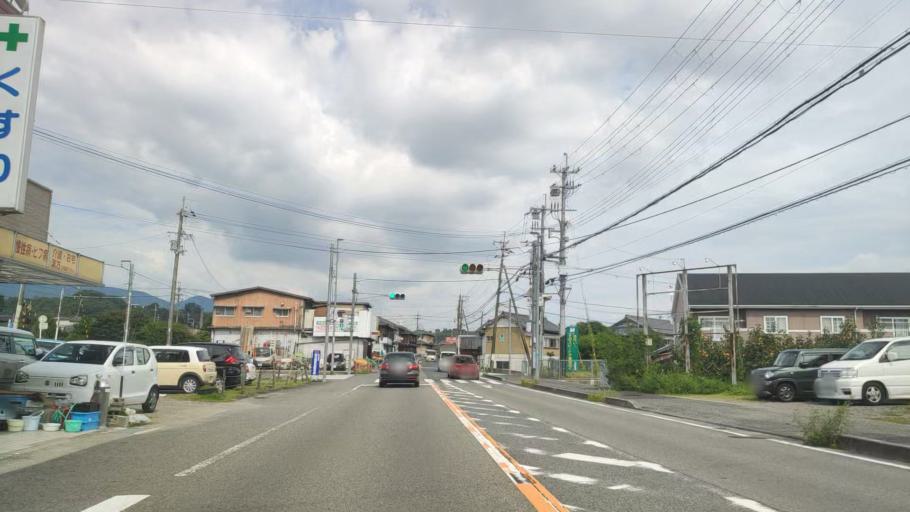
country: JP
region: Wakayama
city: Hashimoto
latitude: 34.3027
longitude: 135.5298
